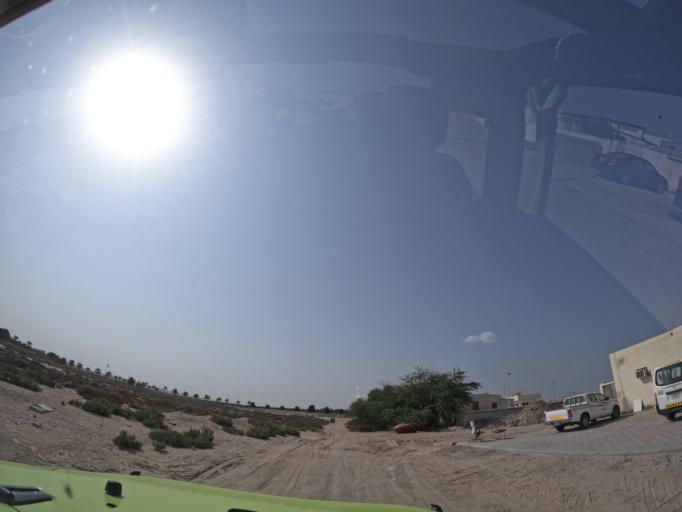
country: AE
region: Umm al Qaywayn
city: Umm al Qaywayn
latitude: 25.4787
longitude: 55.5282
